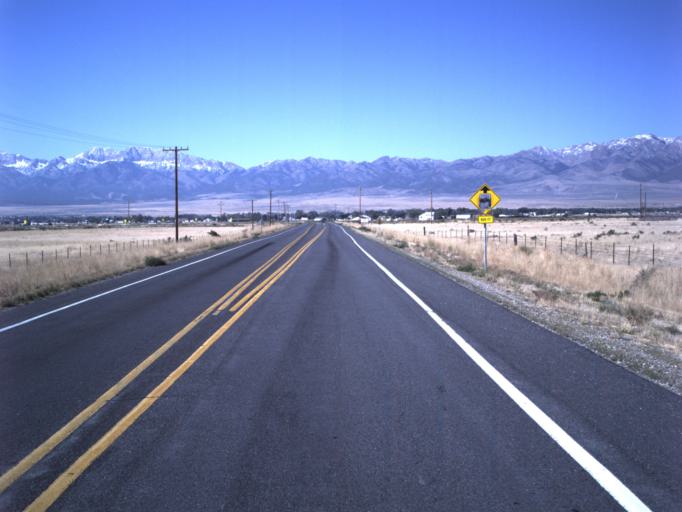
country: US
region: Utah
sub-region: Tooele County
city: Grantsville
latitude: 40.6025
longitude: -112.4005
